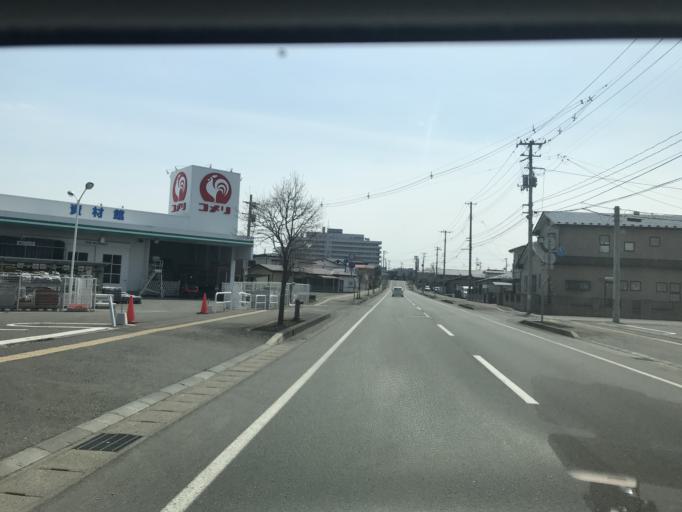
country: JP
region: Iwate
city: Mizusawa
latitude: 39.1271
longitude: 141.1354
